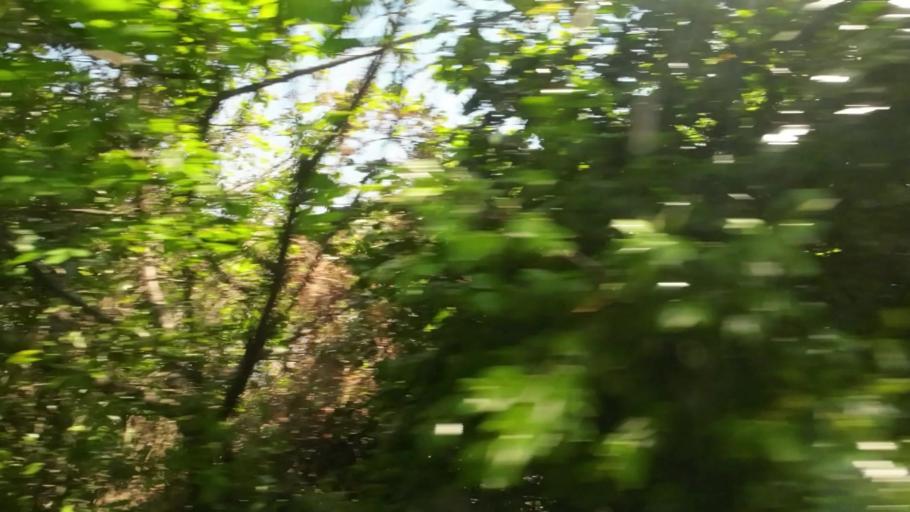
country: JP
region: Ehime
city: Niihama
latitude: 33.9704
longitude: 133.3563
